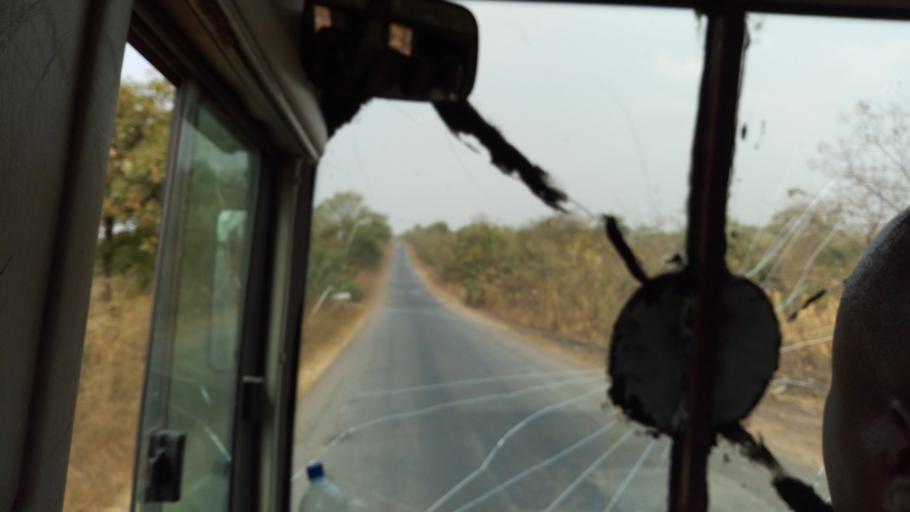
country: TG
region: Centrale
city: Sokode
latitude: 9.0775
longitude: 1.1346
